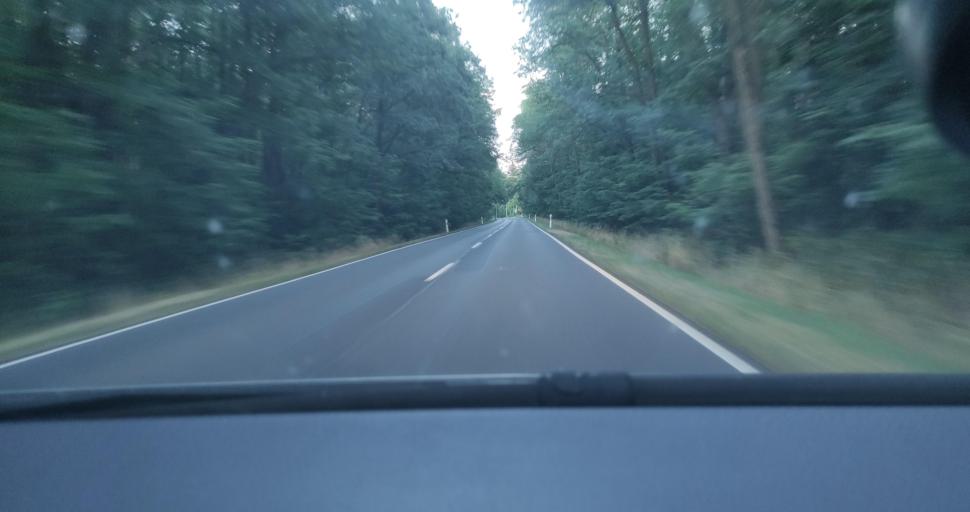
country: DE
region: Brandenburg
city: Forst
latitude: 51.7229
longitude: 14.5601
